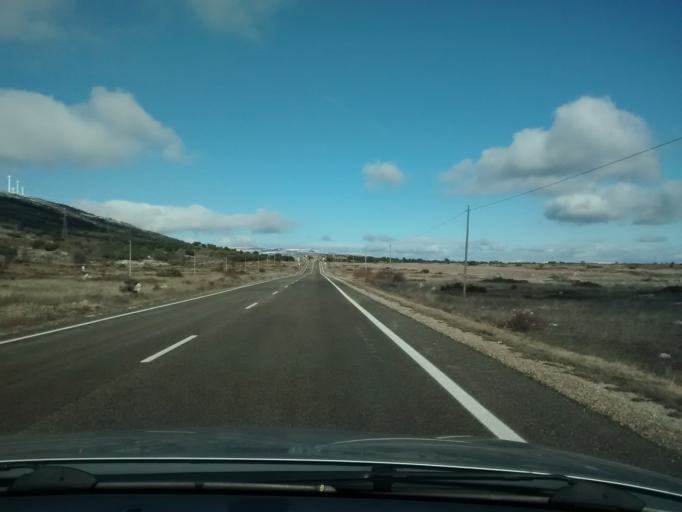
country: ES
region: Castille and Leon
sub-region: Provincia de Burgos
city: Rucandio
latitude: 42.8064
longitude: -3.6160
